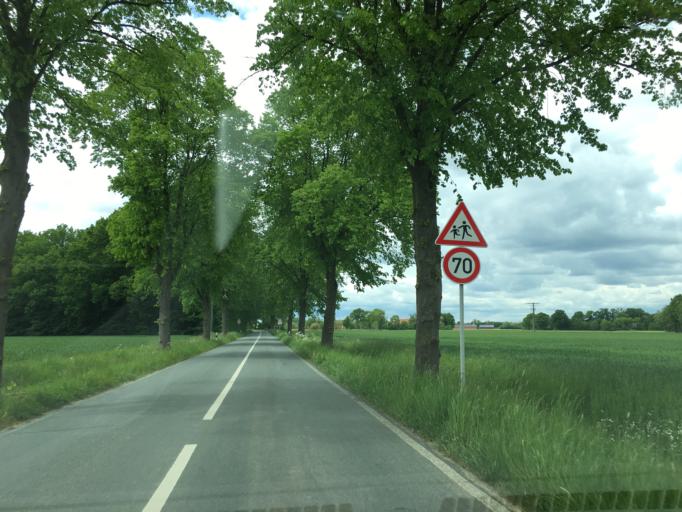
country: DE
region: North Rhine-Westphalia
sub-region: Regierungsbezirk Munster
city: Altenberge
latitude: 51.9865
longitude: 7.5046
